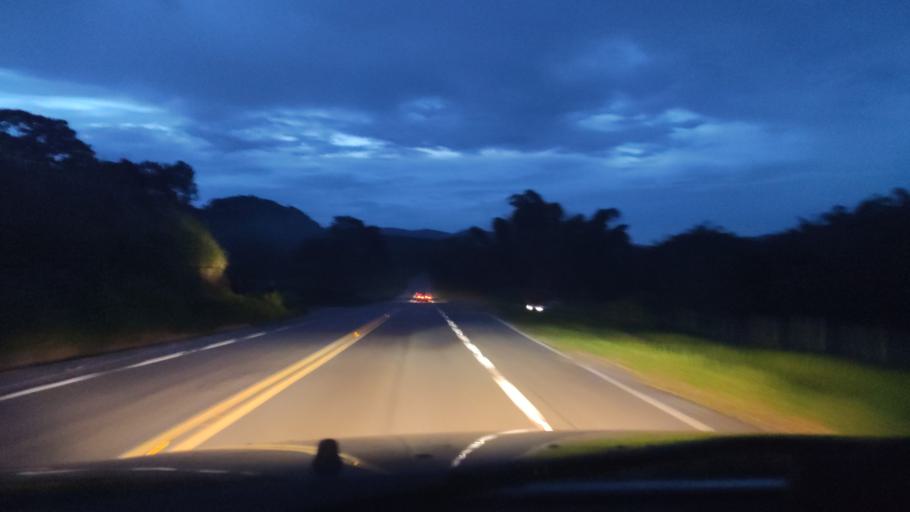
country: BR
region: Sao Paulo
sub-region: Socorro
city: Socorro
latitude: -22.5604
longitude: -46.5936
